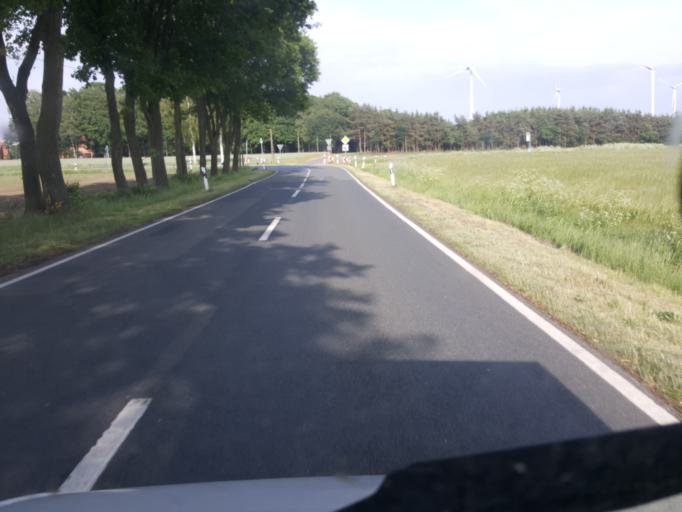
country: DE
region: Lower Saxony
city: Uchte
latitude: 52.5414
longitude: 8.9298
